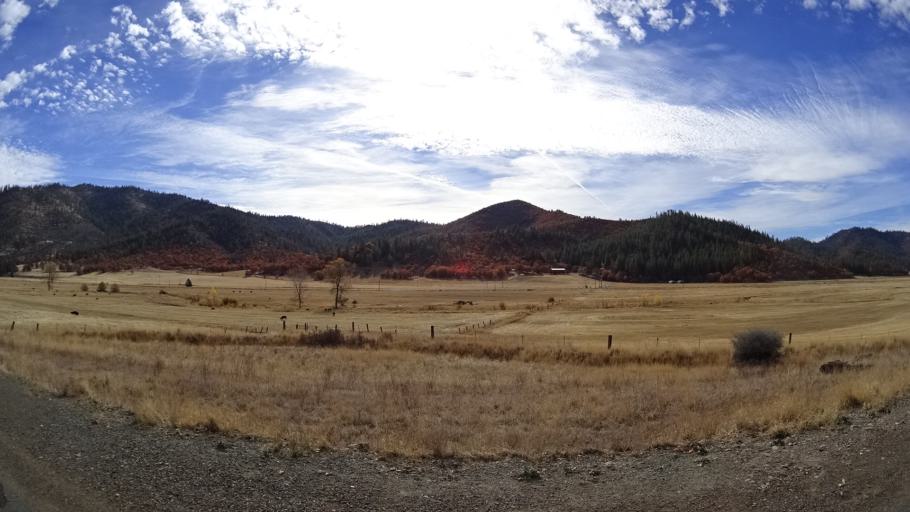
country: US
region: California
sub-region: Siskiyou County
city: Yreka
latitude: 41.6287
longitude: -122.7668
